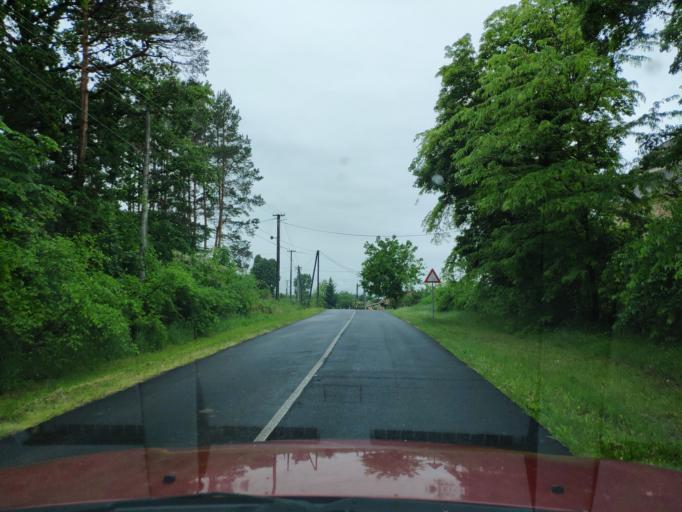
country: SK
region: Kosicky
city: Cierna nad Tisou
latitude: 48.4029
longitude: 22.0568
